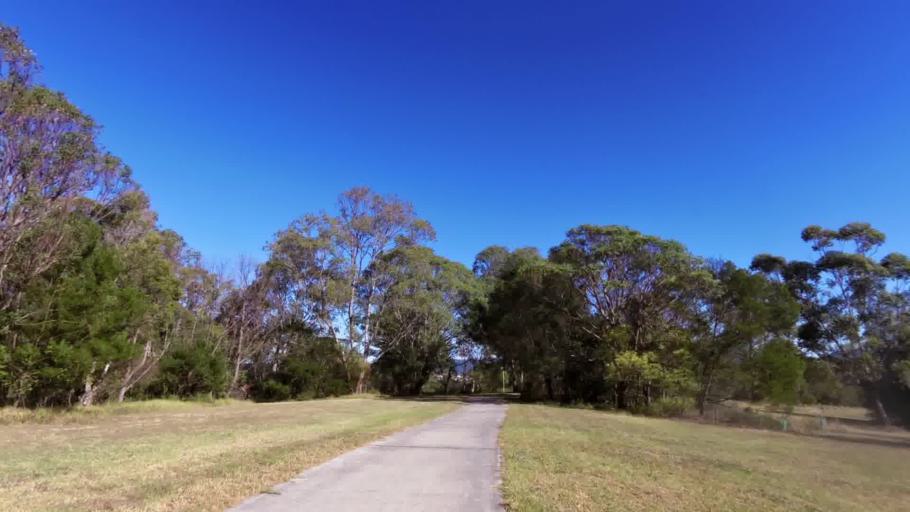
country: AU
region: New South Wales
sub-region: Wollongong
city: Berkeley
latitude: -34.4878
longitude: 150.8370
